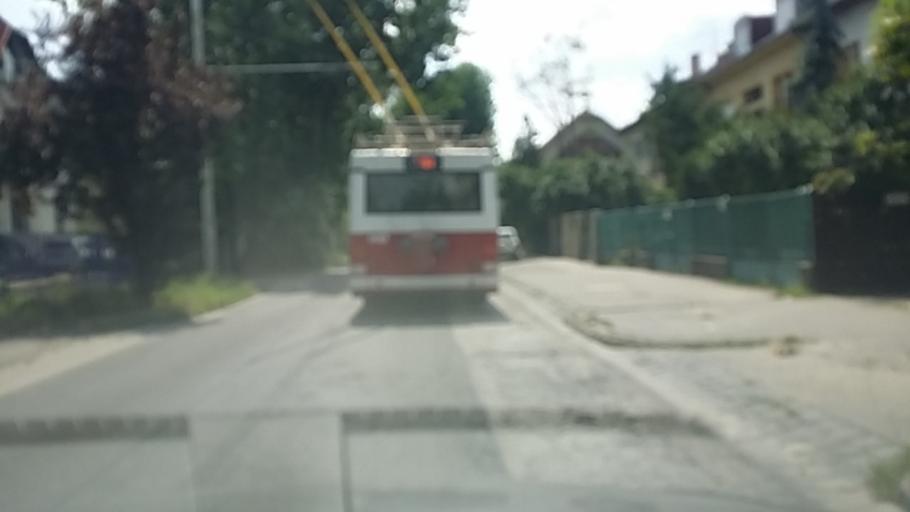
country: HU
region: Budapest
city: Budapest XIV. keruelet
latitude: 47.5260
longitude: 19.0951
